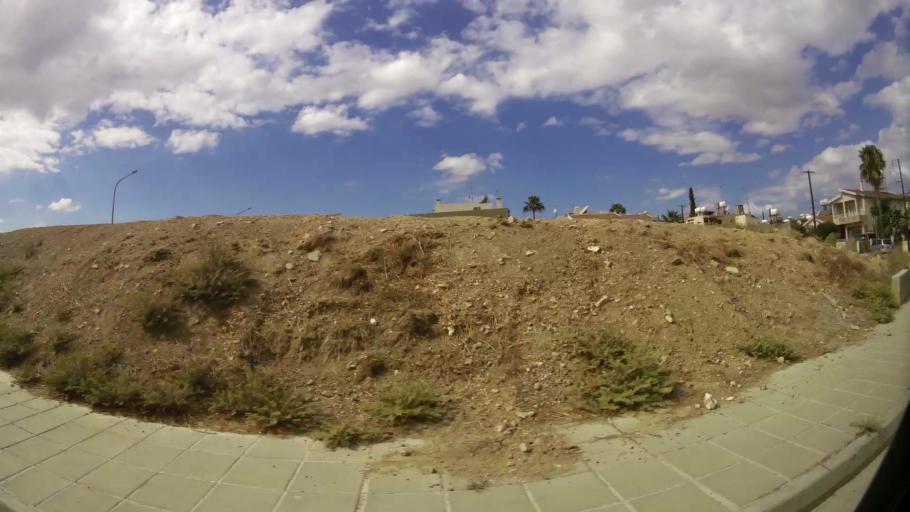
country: CY
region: Lefkosia
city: Nicosia
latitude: 35.1755
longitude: 33.3890
